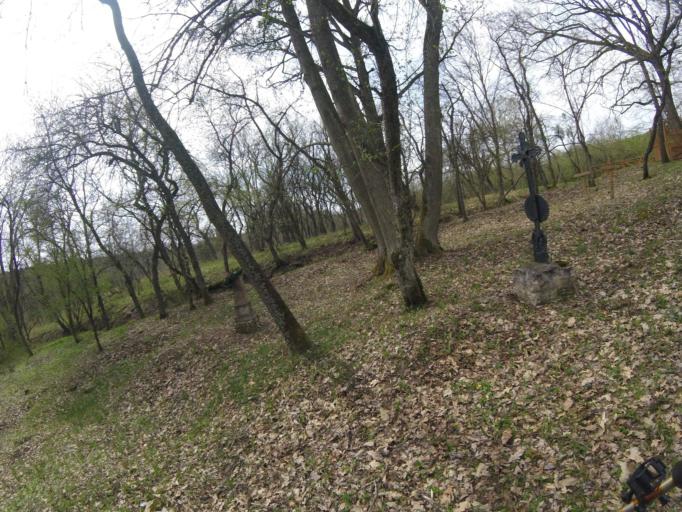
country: SK
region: Kosicky
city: Roznava
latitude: 48.5439
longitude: 20.6429
